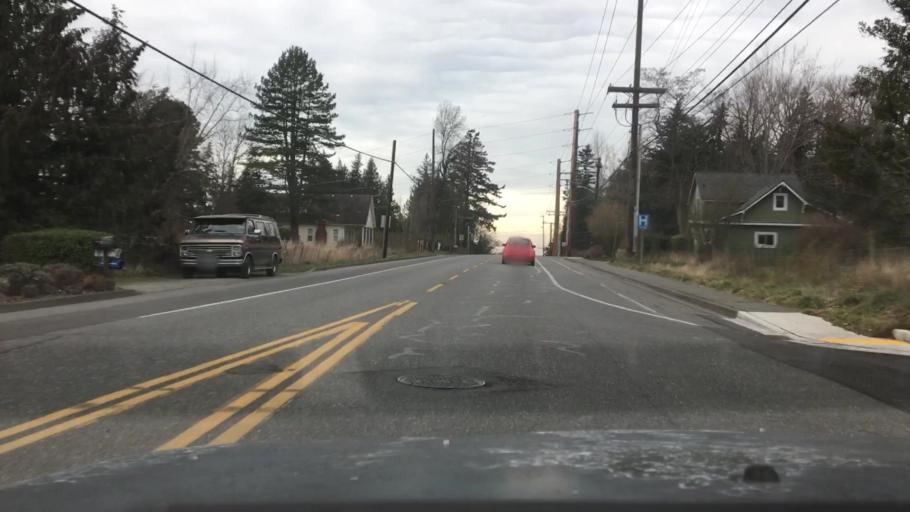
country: US
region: Washington
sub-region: Skagit County
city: Mount Vernon
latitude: 48.4065
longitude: -122.3242
